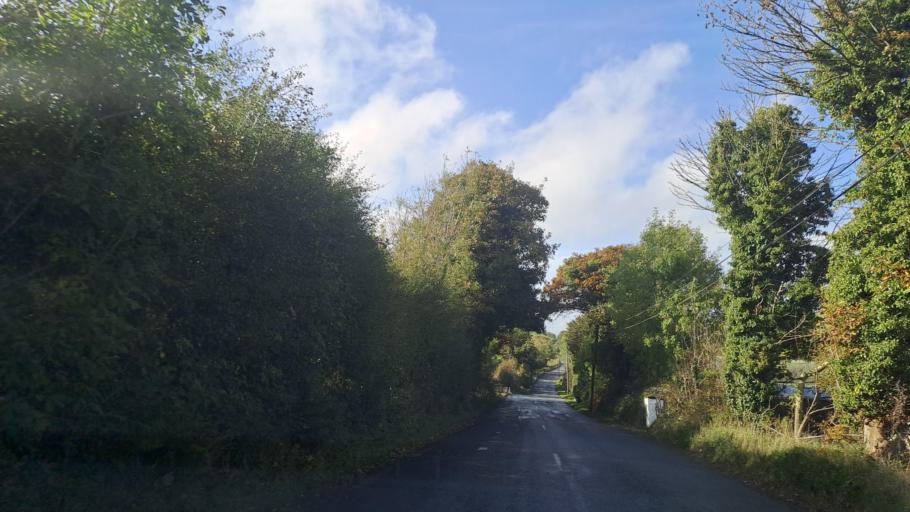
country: IE
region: Ulster
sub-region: An Cabhan
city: Bailieborough
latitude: 54.0236
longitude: -6.9432
